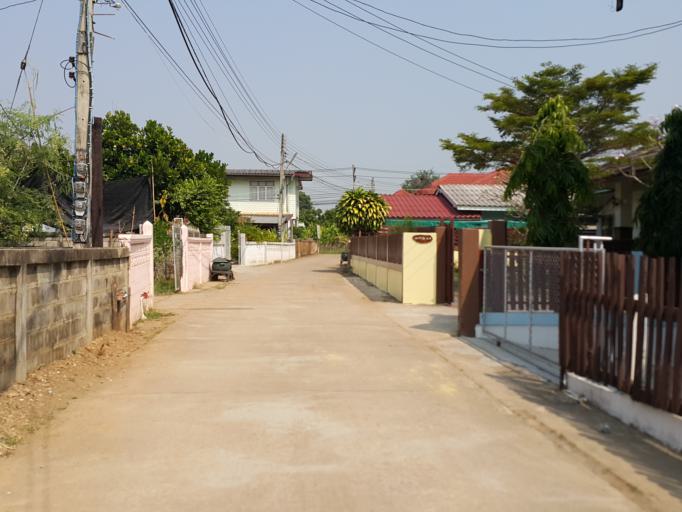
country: TH
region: Sukhothai
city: Thung Saliam
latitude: 17.3242
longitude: 99.5336
